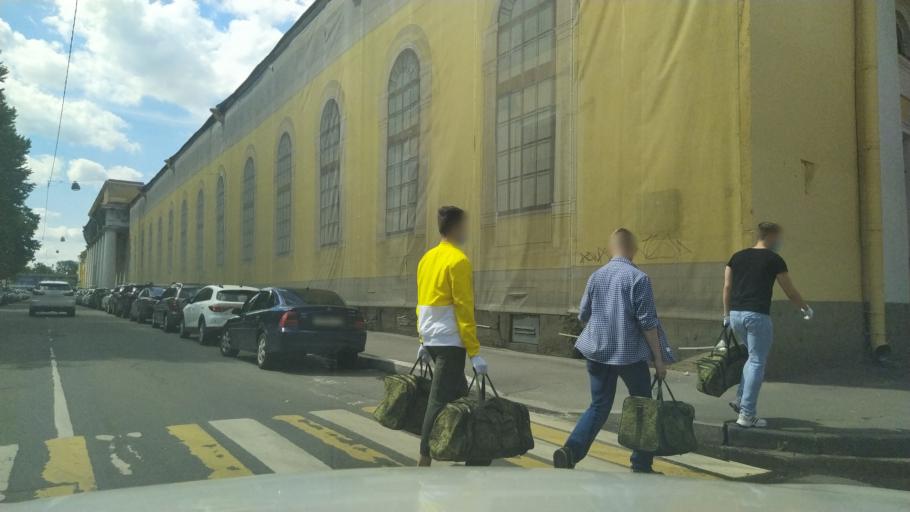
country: RU
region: St.-Petersburg
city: Petrogradka
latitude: 59.9582
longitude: 30.2846
